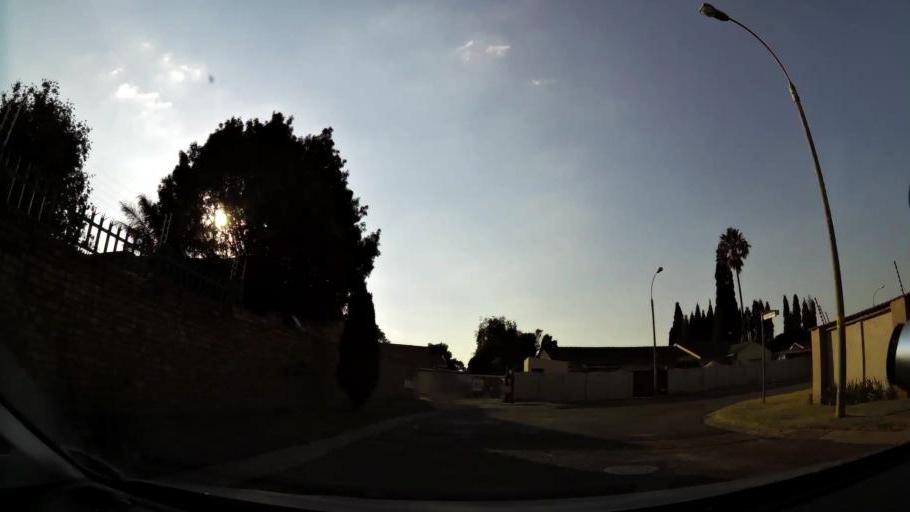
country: ZA
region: Gauteng
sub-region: City of Johannesburg Metropolitan Municipality
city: Modderfontein
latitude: -26.0666
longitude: 28.2192
